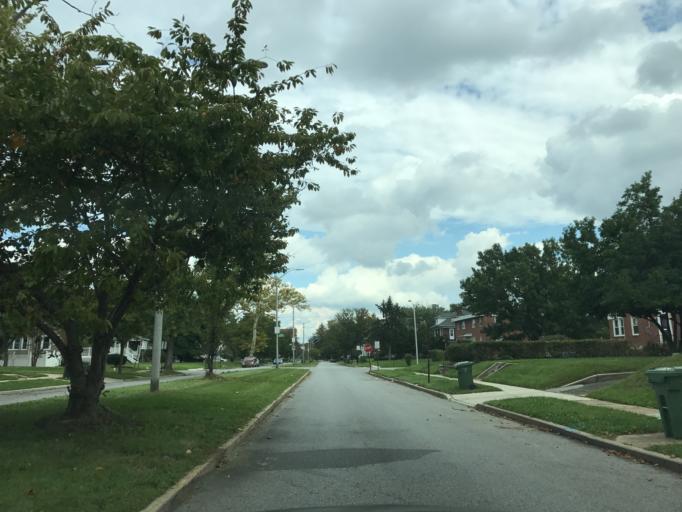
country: US
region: Maryland
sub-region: Baltimore County
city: Lochearn
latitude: 39.3304
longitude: -76.6768
